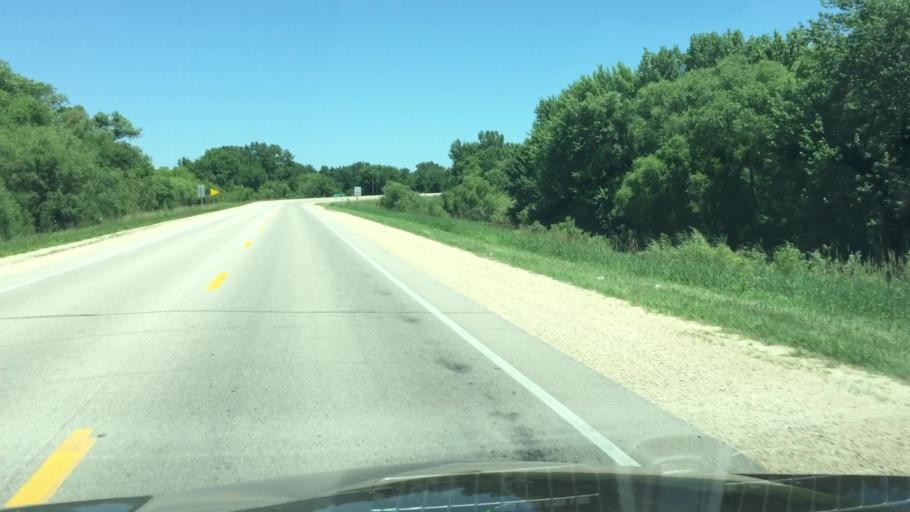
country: US
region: Iowa
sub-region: Cedar County
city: Mechanicsville
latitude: 42.0039
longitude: -91.1418
